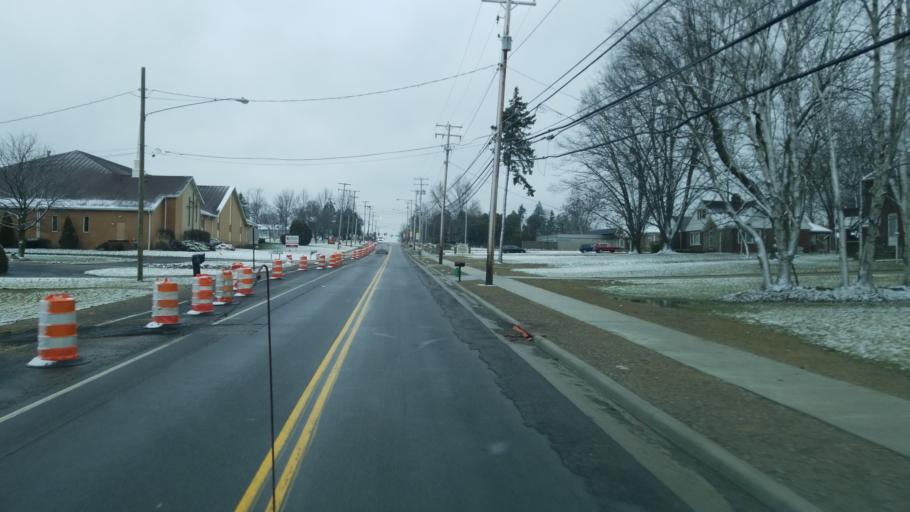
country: US
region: Ohio
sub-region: Summit County
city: Norton
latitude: 41.0296
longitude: -81.6381
